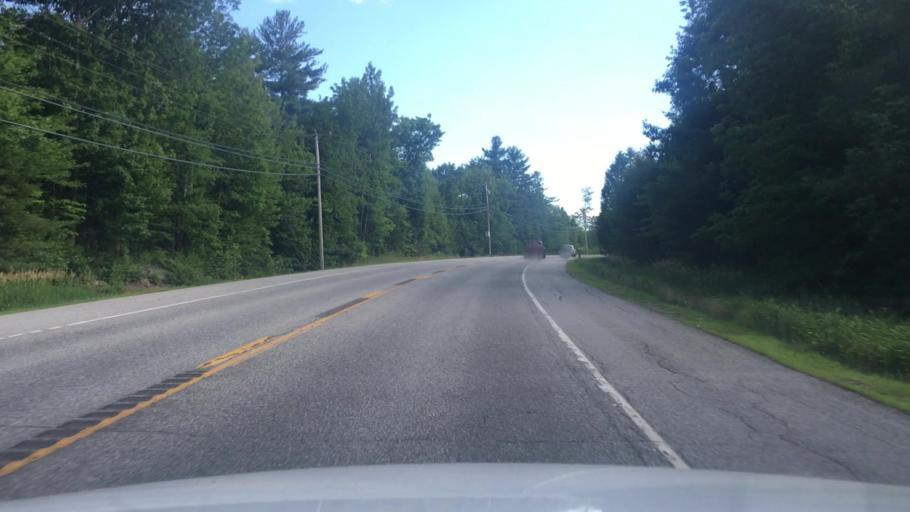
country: US
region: Maine
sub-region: Androscoggin County
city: Livermore Falls
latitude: 44.4510
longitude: -70.1985
